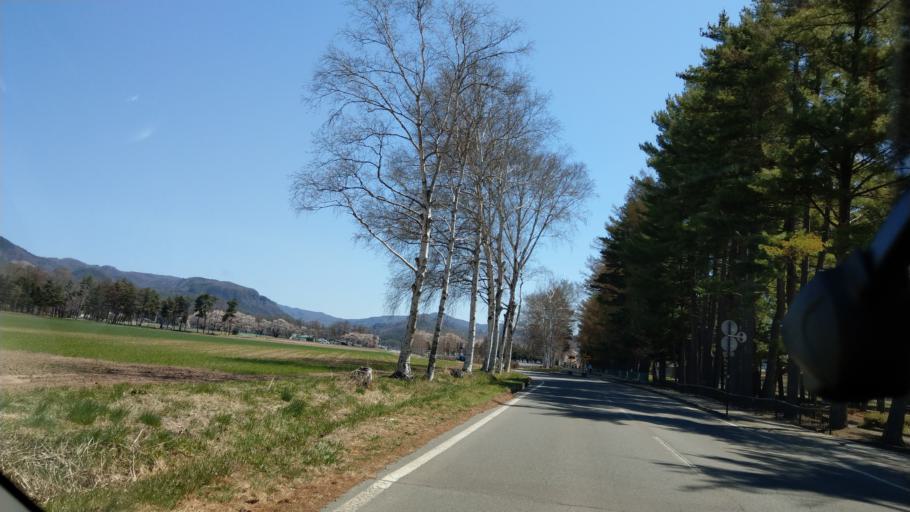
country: JP
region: Nagano
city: Saku
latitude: 36.2566
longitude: 138.4871
